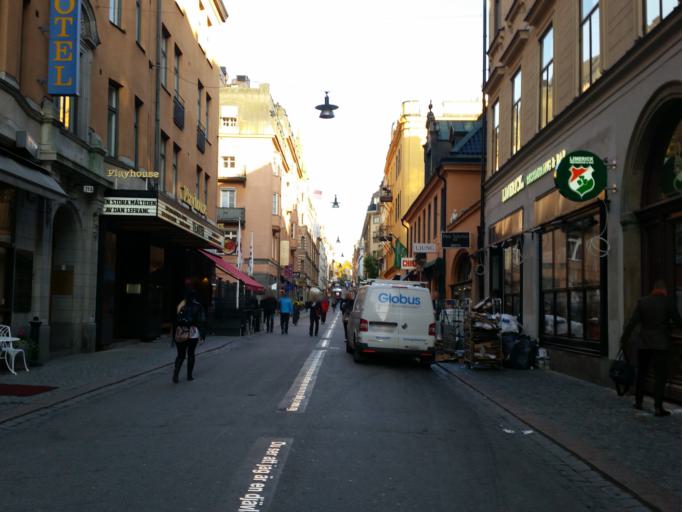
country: SE
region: Stockholm
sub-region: Stockholms Kommun
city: Stockholm
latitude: 59.3357
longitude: 18.0596
